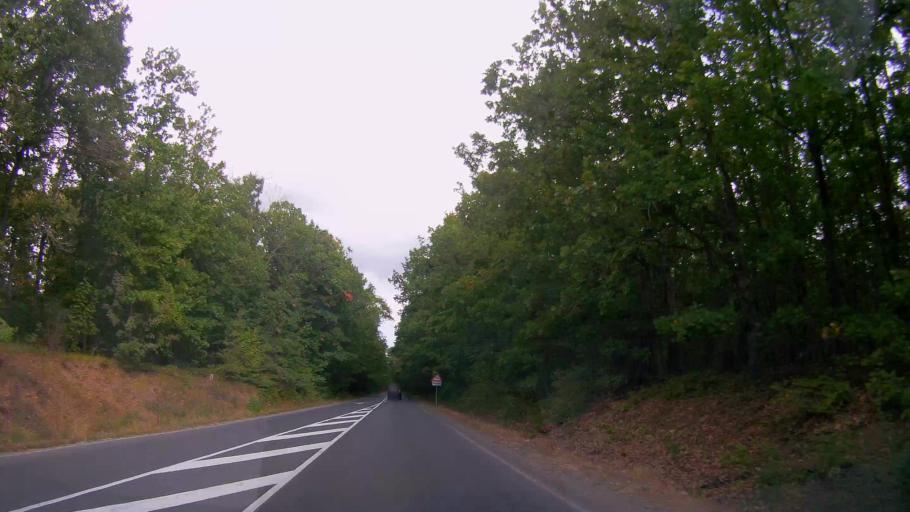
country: BG
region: Burgas
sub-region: Obshtina Primorsko
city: Primorsko
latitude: 42.2767
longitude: 27.7400
